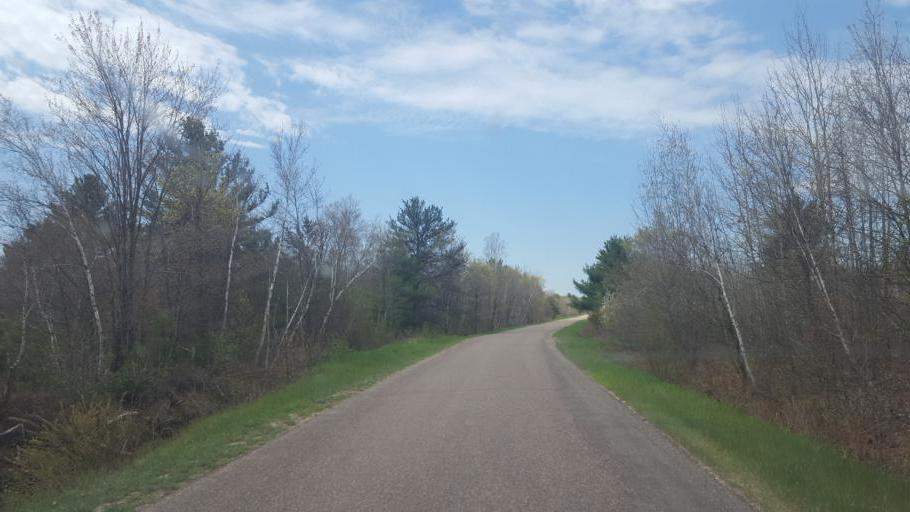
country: US
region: Wisconsin
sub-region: Clark County
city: Neillsville
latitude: 44.2929
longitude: -90.4812
